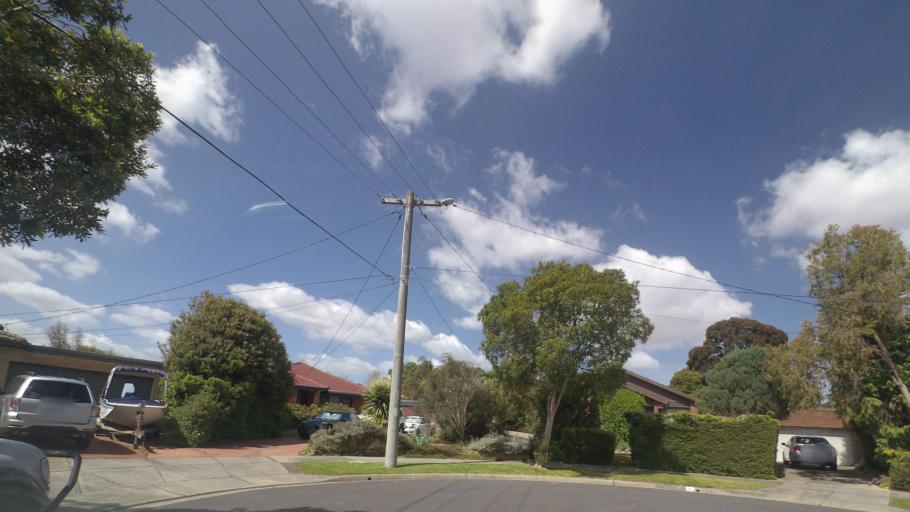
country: AU
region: Victoria
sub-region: Maroondah
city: Heathmont
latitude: -37.8392
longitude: 145.2528
